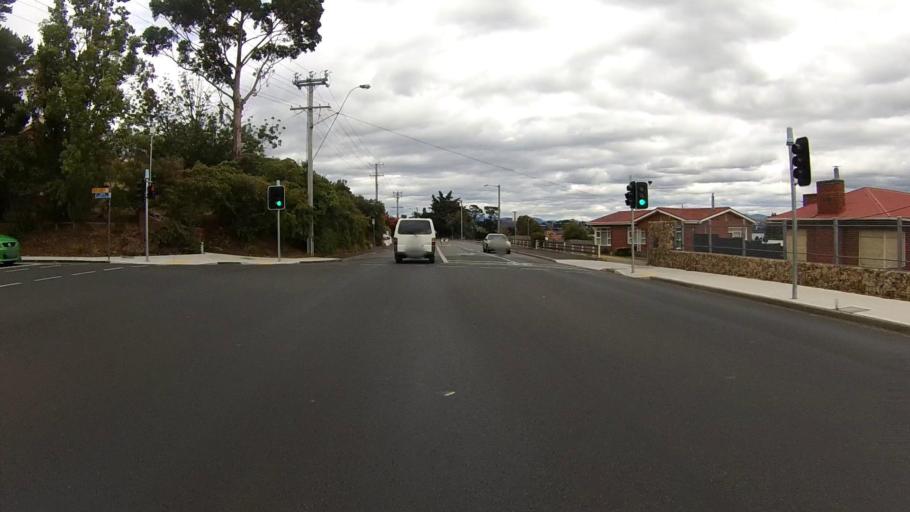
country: AU
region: Tasmania
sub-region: Glenorchy
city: Berriedale
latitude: -42.8225
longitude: 147.2638
